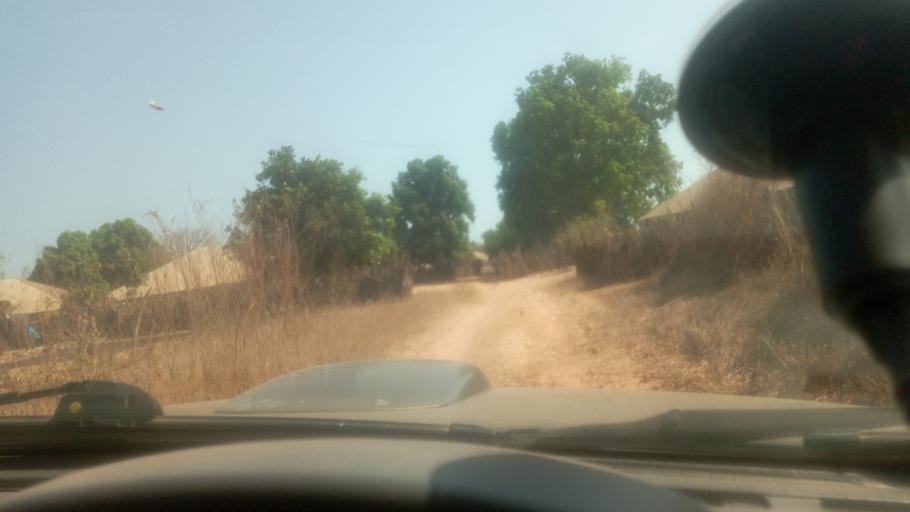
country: GW
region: Oio
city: Farim
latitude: 12.4625
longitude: -15.4070
